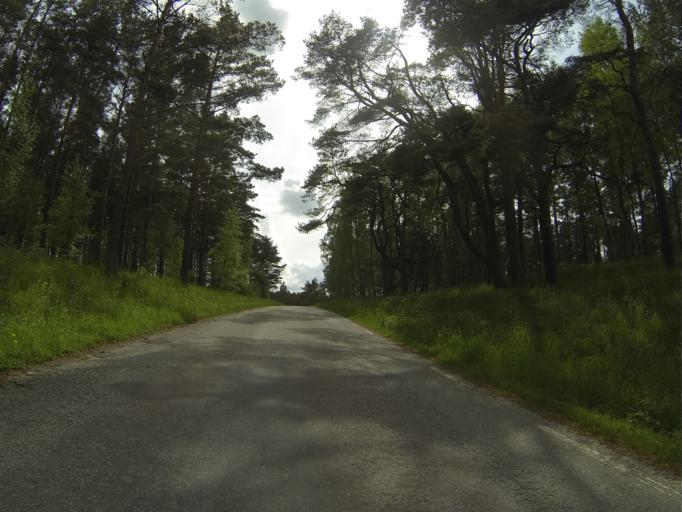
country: SE
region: Skane
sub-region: Sjobo Kommun
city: Blentarp
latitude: 55.6598
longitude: 13.6146
